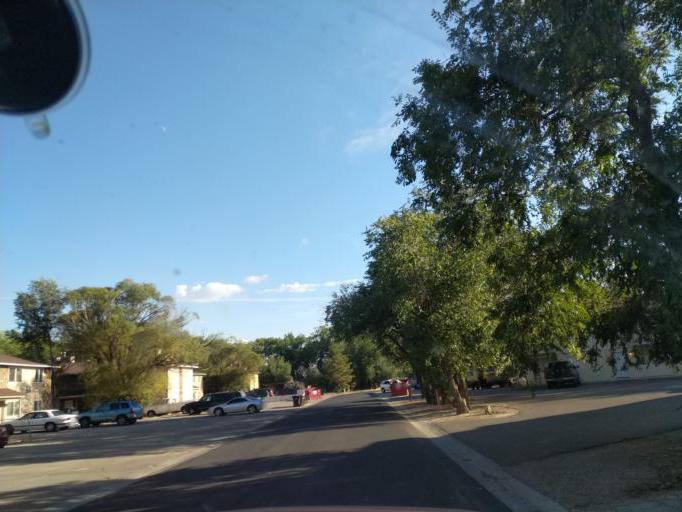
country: US
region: Colorado
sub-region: Mesa County
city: Clifton
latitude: 39.0724
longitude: -108.4569
